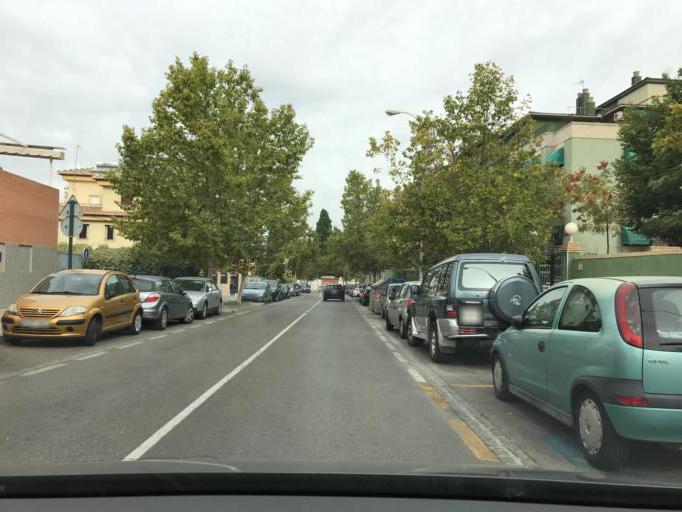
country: ES
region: Andalusia
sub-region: Provincia de Granada
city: Huetor Vega
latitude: 37.1622
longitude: -3.5901
